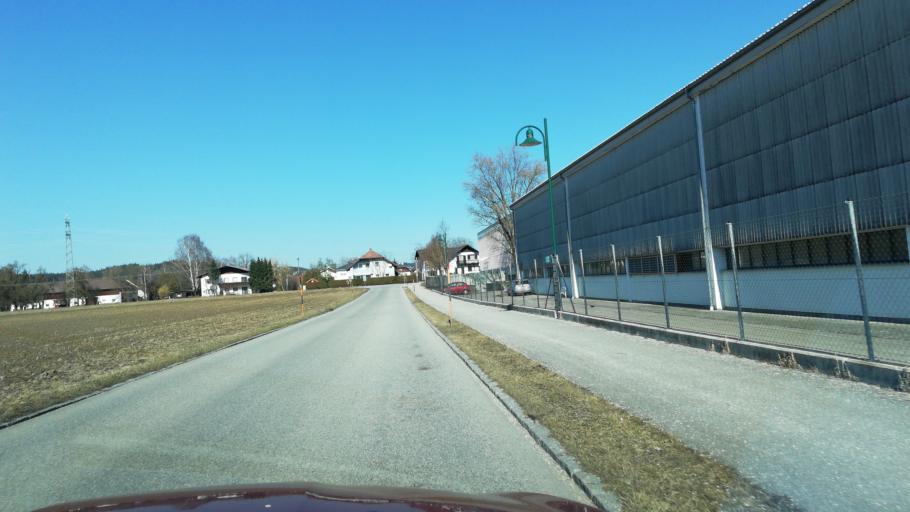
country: AT
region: Upper Austria
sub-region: Politischer Bezirk Vocklabruck
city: Oberndorf bei Schwanenstadt
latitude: 48.0537
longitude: 13.7635
